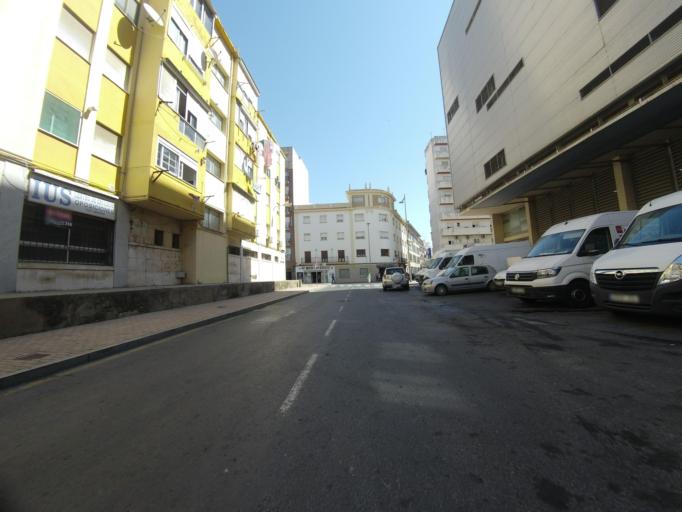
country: ES
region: Andalusia
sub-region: Provincia de Huelva
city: Huelva
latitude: 37.2550
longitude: -6.9562
